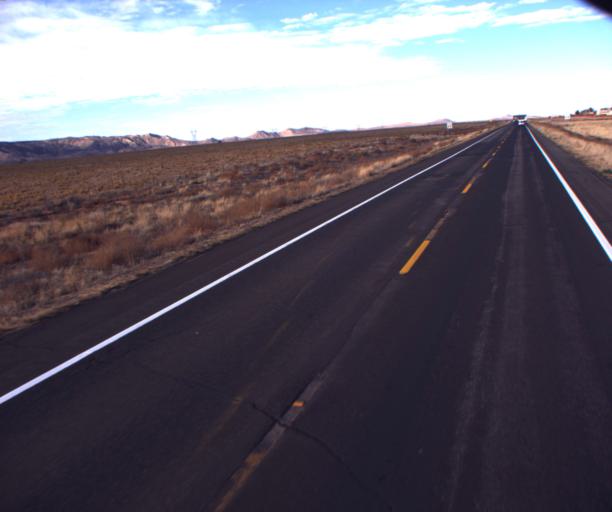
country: US
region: Arizona
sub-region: Apache County
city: Lukachukai
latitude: 36.9606
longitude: -109.3752
